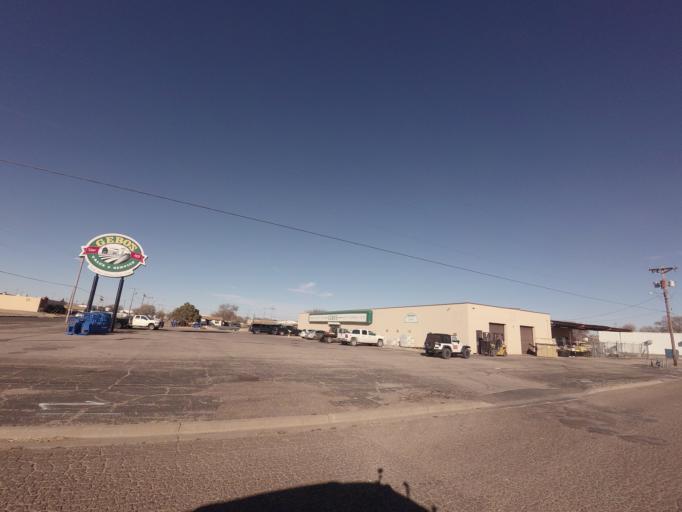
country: US
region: New Mexico
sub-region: Curry County
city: Clovis
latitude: 34.3986
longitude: -103.1874
